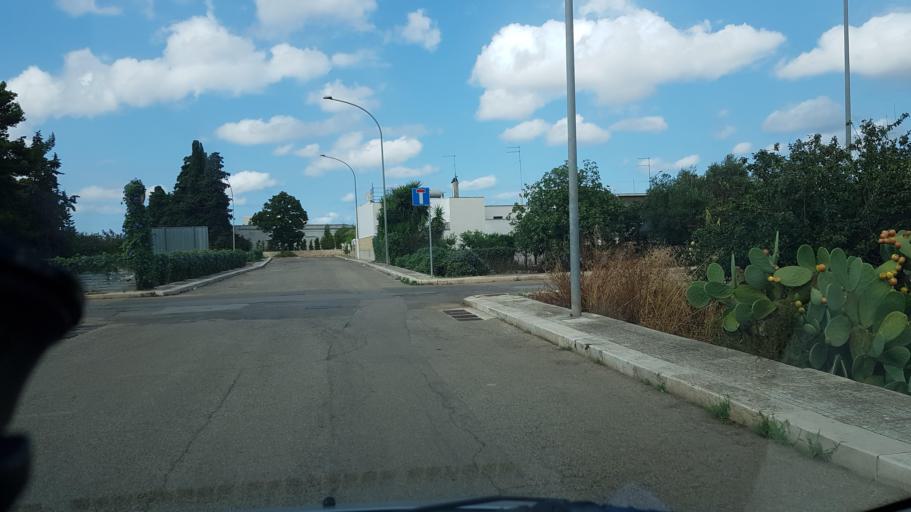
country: IT
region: Apulia
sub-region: Provincia di Brindisi
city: San Vito dei Normanni
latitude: 40.6569
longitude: 17.7158
